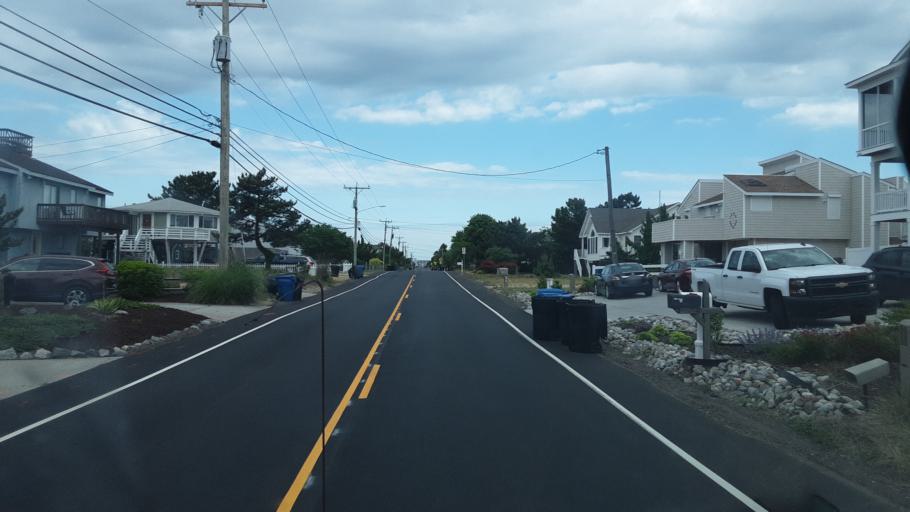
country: US
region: Virginia
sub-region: City of Virginia Beach
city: Virginia Beach
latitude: 36.7296
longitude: -75.9390
